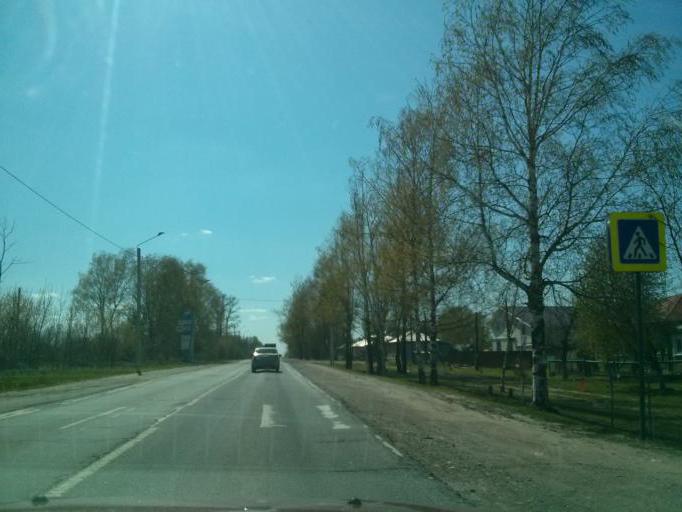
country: RU
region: Nizjnij Novgorod
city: Bogorodsk
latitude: 56.0629
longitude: 43.4224
